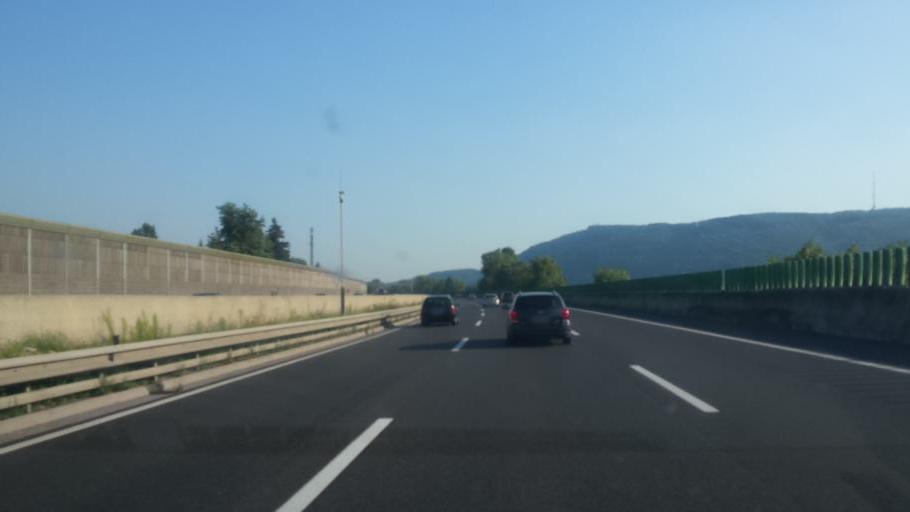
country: AT
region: Lower Austria
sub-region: Politischer Bezirk Korneuburg
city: Langenzersdorf
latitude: 48.3065
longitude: 16.3450
